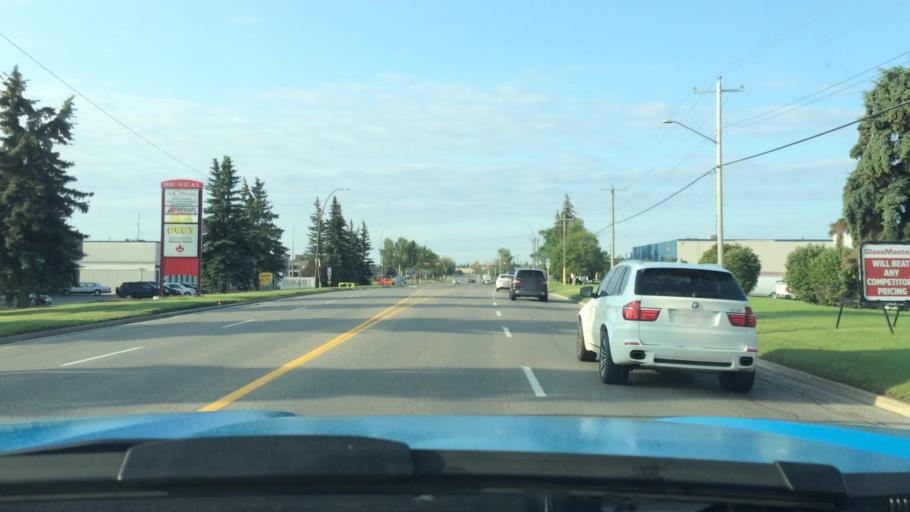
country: CA
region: Alberta
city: Calgary
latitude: 51.0837
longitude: -114.0117
